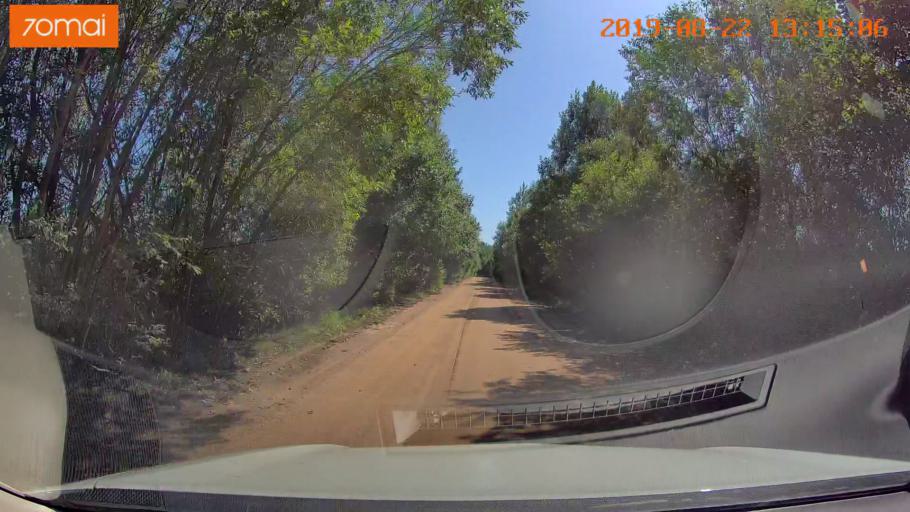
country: BY
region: Minsk
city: Prawdzinski
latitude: 53.2627
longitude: 27.8931
